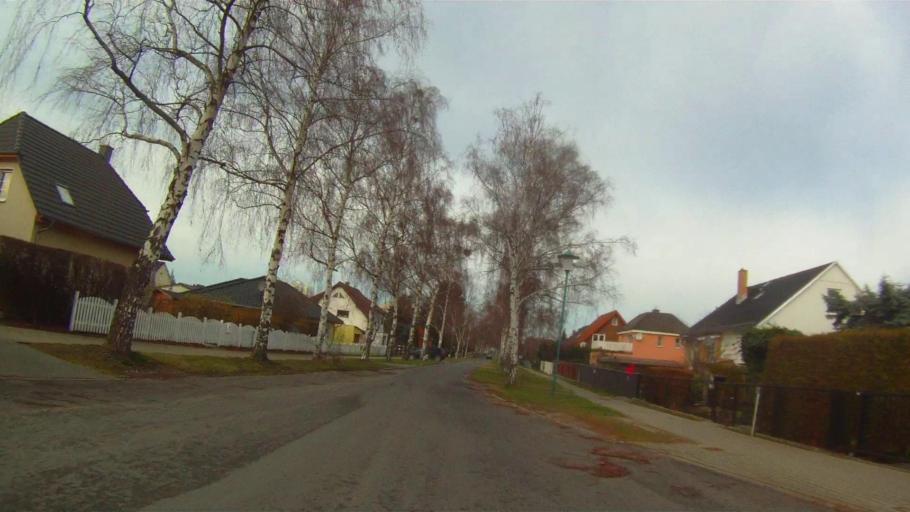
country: DE
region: Berlin
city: Gropiusstadt
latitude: 52.4134
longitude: 13.4525
